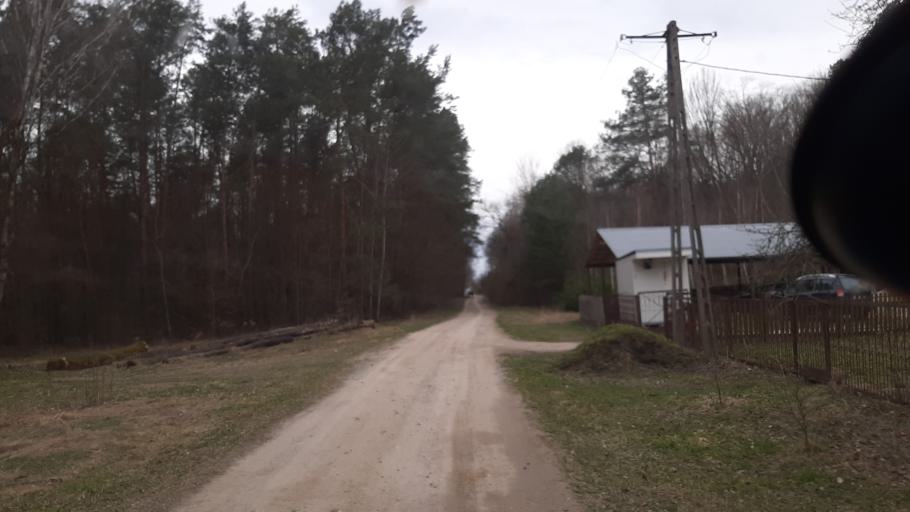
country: PL
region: Lublin Voivodeship
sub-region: Powiat lubartowski
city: Abramow
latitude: 51.4450
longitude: 22.3397
